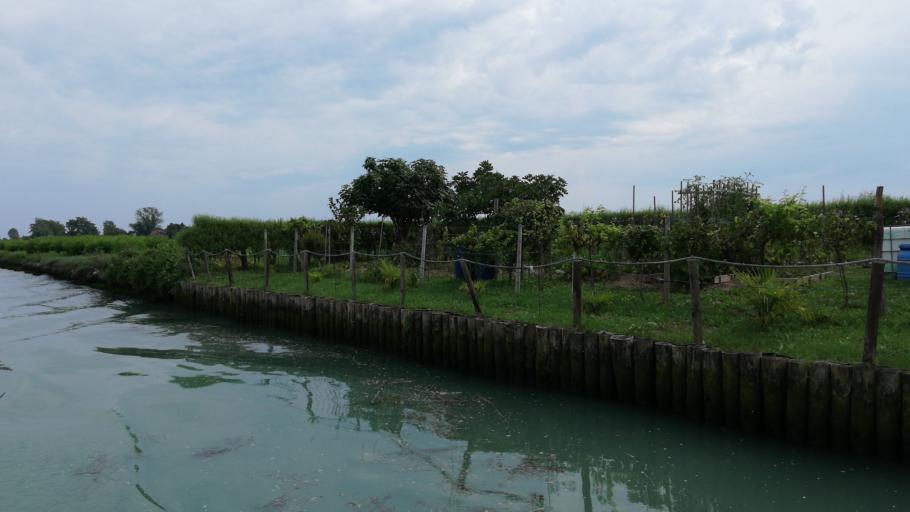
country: IT
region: Veneto
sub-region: Provincia di Venezia
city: Caorle
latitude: 45.6245
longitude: 12.8872
